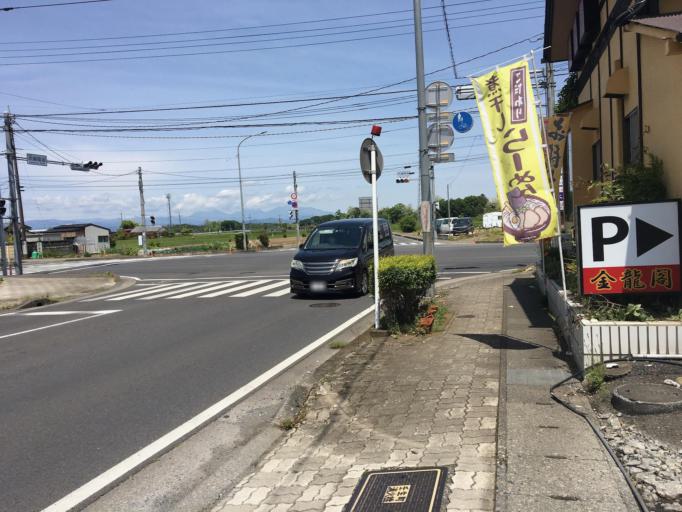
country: JP
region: Tochigi
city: Mibu
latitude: 36.4347
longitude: 139.8021
